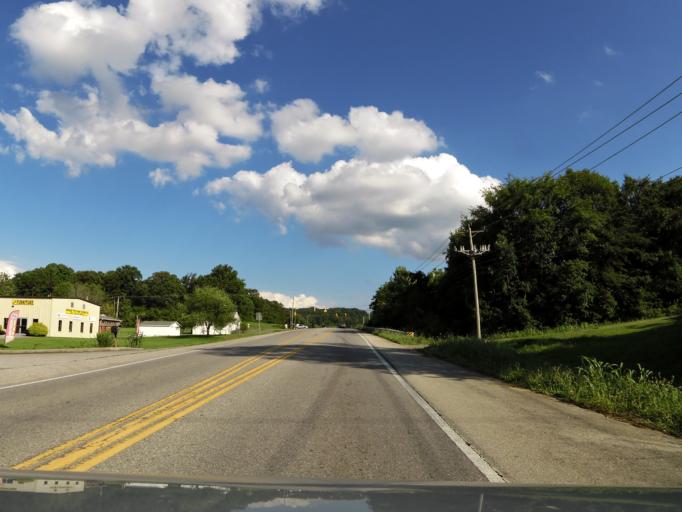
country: US
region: Tennessee
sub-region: Blount County
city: Maryville
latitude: 35.7311
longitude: -84.0333
